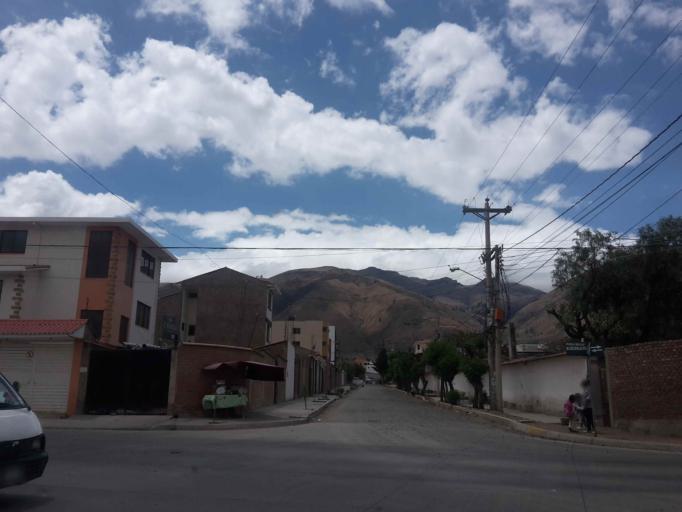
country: BO
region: Cochabamba
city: Cochabamba
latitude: -17.3457
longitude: -66.1968
